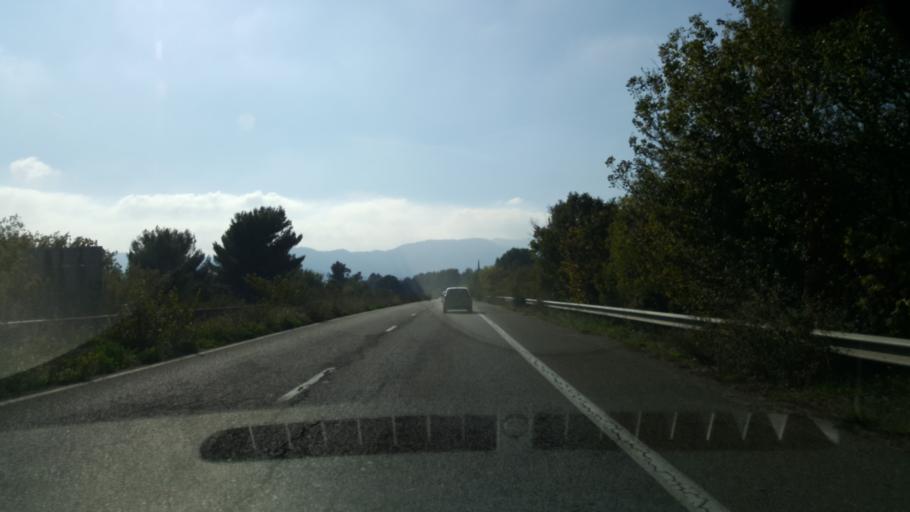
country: FR
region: Provence-Alpes-Cote d'Azur
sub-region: Departement des Bouches-du-Rhone
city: Aubagne
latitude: 43.2988
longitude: 5.5623
